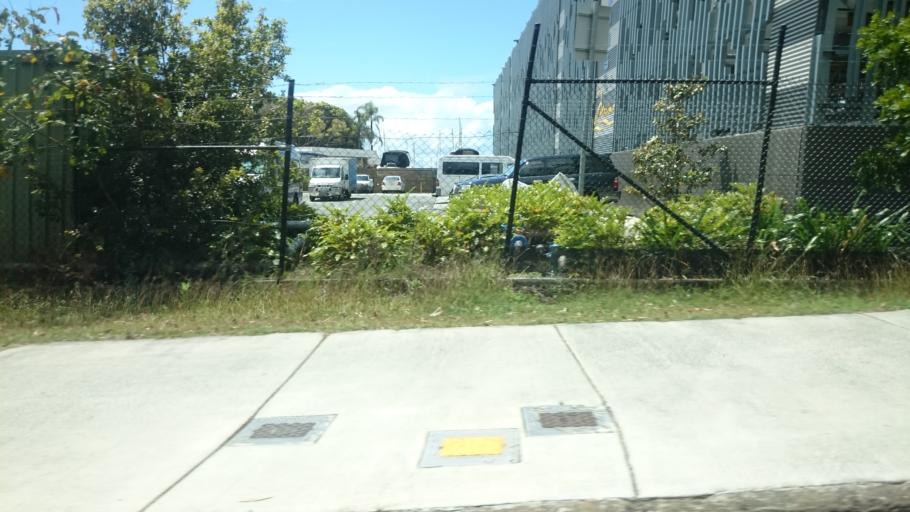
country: AU
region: Queensland
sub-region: Brisbane
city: Manly West
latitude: -27.4600
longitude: 153.1881
